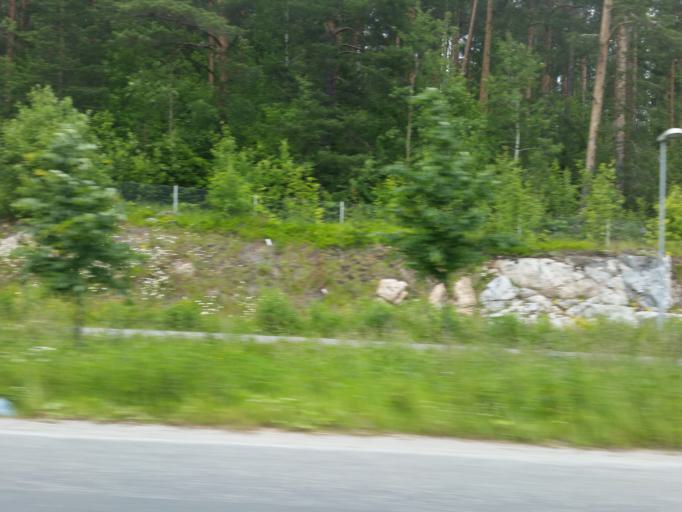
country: FI
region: Northern Savo
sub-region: Kuopio
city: Kuopio
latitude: 62.8821
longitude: 27.6519
